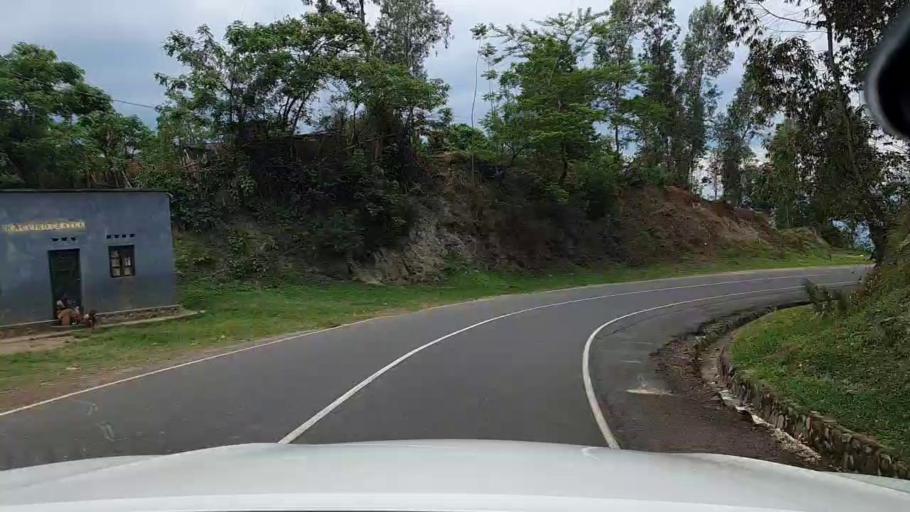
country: RW
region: Western Province
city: Cyangugu
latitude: -2.6579
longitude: 28.9780
